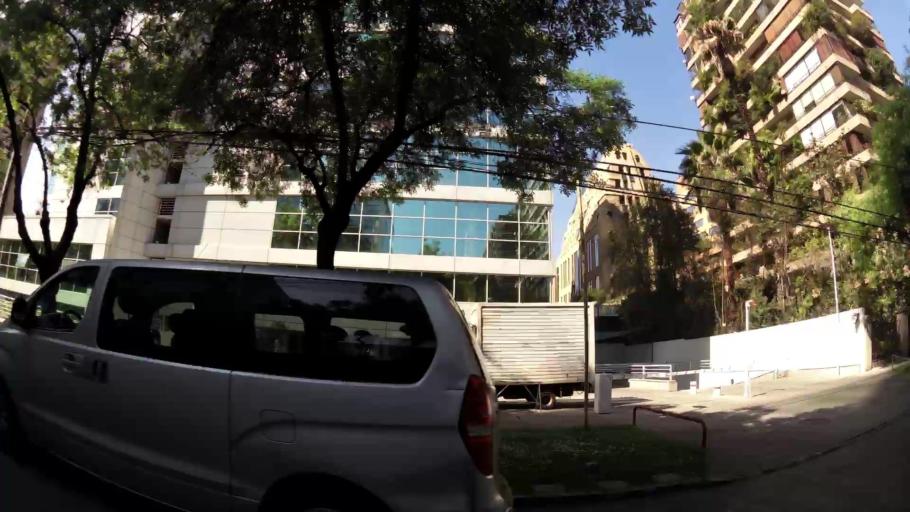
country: CL
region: Santiago Metropolitan
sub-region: Provincia de Santiago
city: Villa Presidente Frei, Nunoa, Santiago, Chile
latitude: -33.4158
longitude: -70.5878
